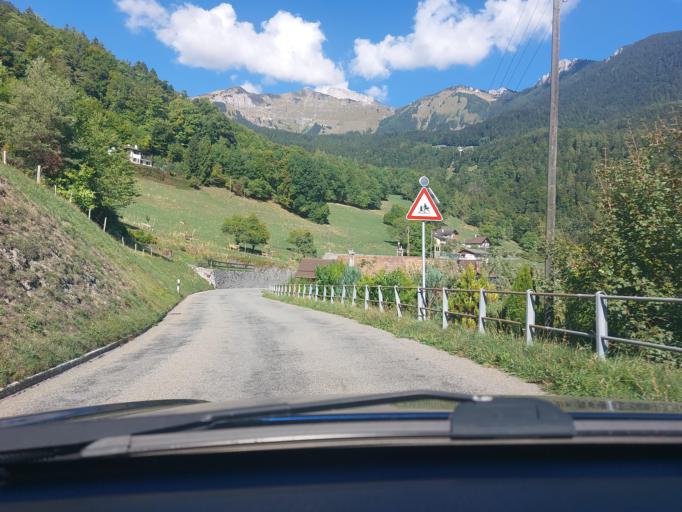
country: CH
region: Vaud
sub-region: Aigle District
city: Aigle
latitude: 46.3424
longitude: 6.9593
